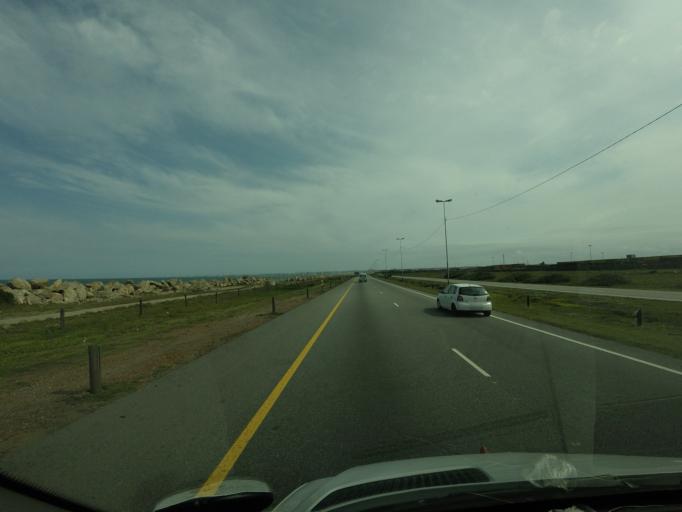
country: ZA
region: Eastern Cape
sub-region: Nelson Mandela Bay Metropolitan Municipality
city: Port Elizabeth
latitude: -33.8927
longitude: 25.6218
